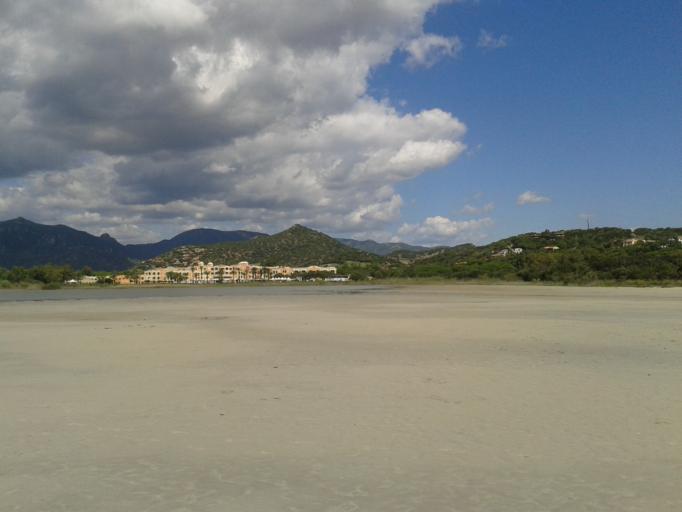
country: IT
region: Sardinia
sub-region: Provincia di Cagliari
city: Villasimius
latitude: 39.1172
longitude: 9.5190
